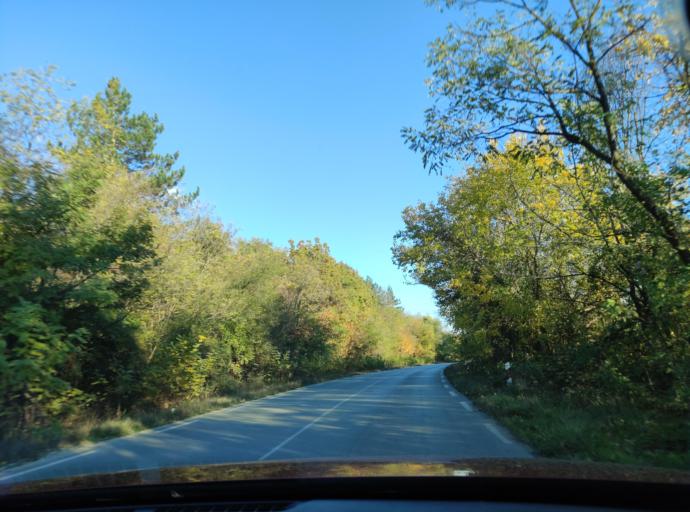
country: BG
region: Montana
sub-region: Obshtina Montana
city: Montana
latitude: 43.4039
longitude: 23.0789
